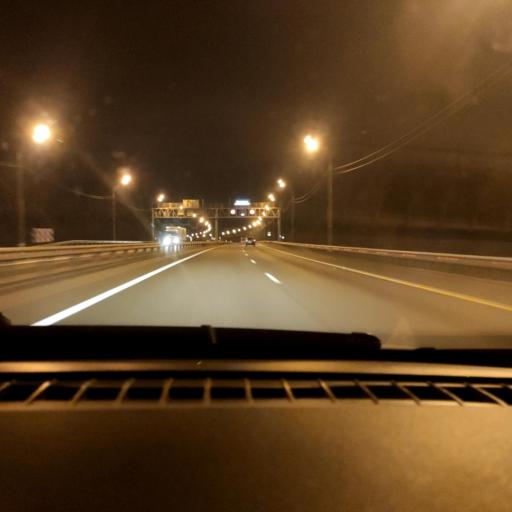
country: RU
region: Lipetsk
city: Khlevnoye
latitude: 52.2518
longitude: 39.0666
